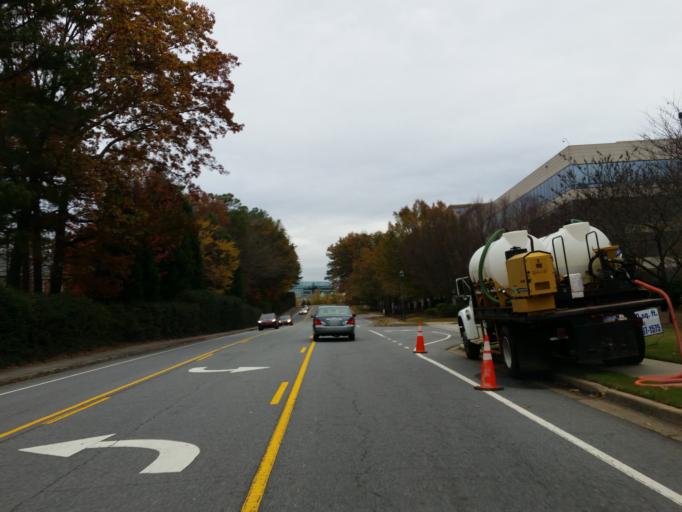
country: US
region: Georgia
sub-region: Fulton County
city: Sandy Springs
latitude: 33.9267
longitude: -84.3598
